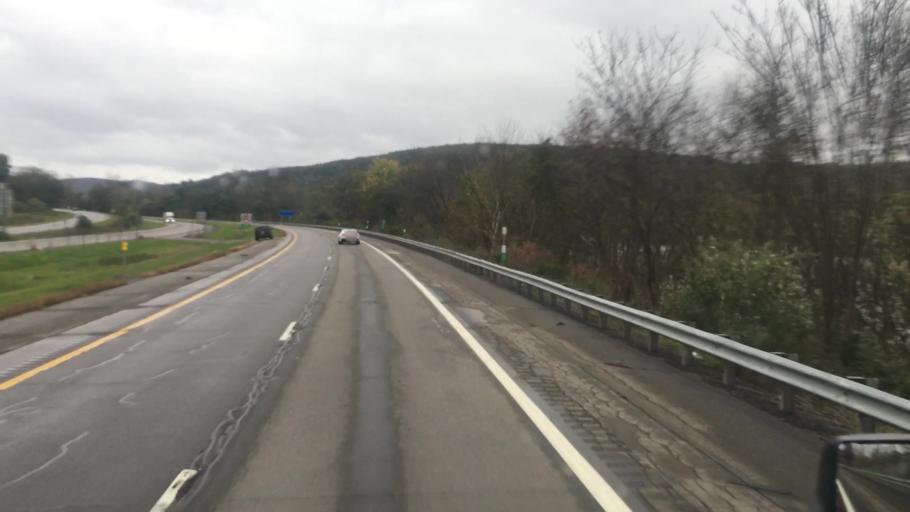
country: US
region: New York
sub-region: Tioga County
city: Owego
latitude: 42.0986
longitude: -76.2396
